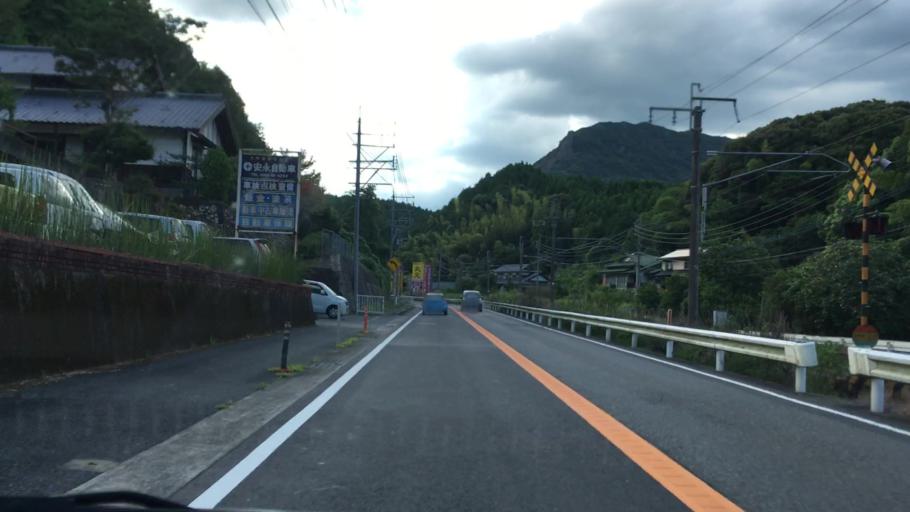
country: JP
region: Saga Prefecture
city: Imaricho-ko
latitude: 33.1917
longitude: 129.9195
